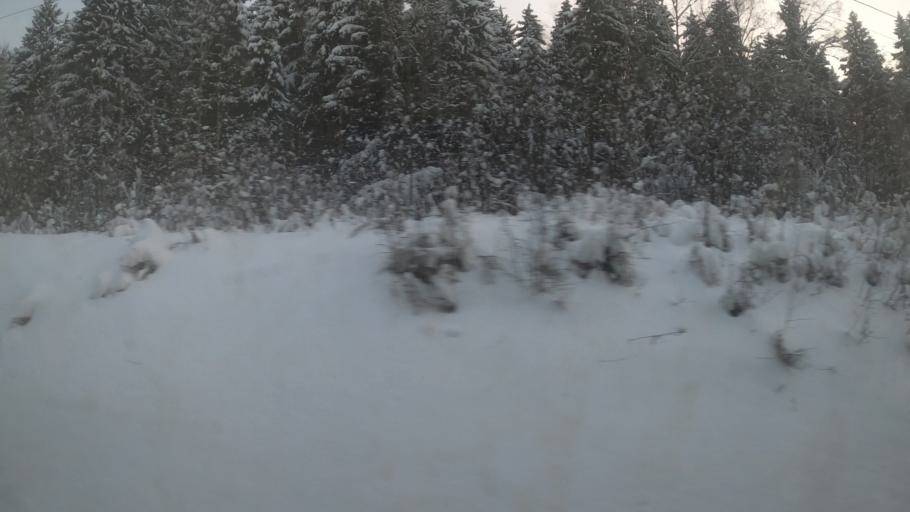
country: RU
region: Moskovskaya
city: Nekrasovskiy
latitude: 56.1140
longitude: 37.5113
